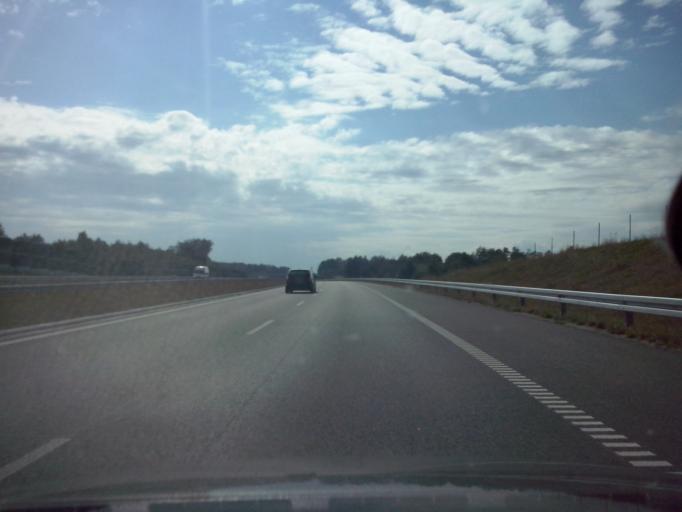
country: PL
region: Lesser Poland Voivodeship
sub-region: Powiat tarnowski
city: Jodlowka-Walki
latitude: 50.0930
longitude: 21.1610
